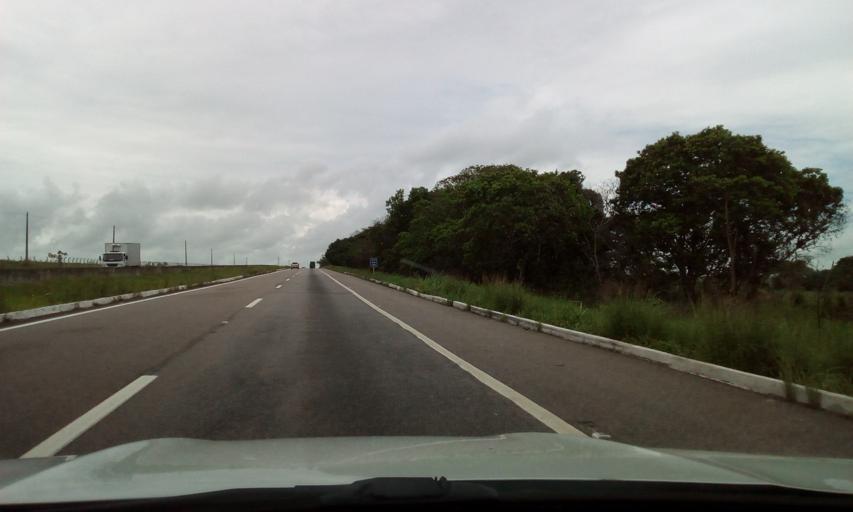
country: BR
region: Paraiba
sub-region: Alhandra
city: Alhandra
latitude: -7.4779
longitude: -34.9791
